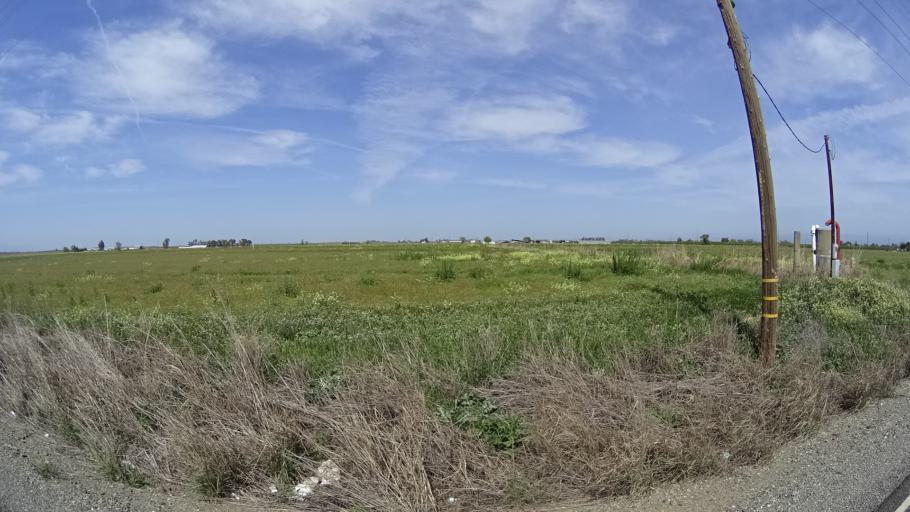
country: US
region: California
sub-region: Glenn County
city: Orland
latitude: 39.7677
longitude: -122.1127
